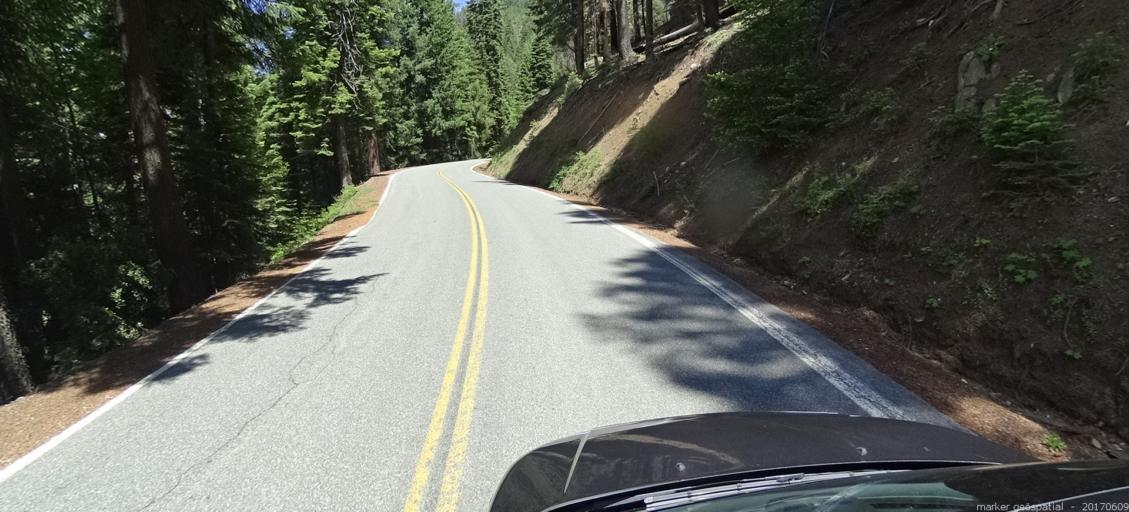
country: US
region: California
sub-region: Siskiyou County
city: Yreka
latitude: 41.3758
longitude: -123.0115
